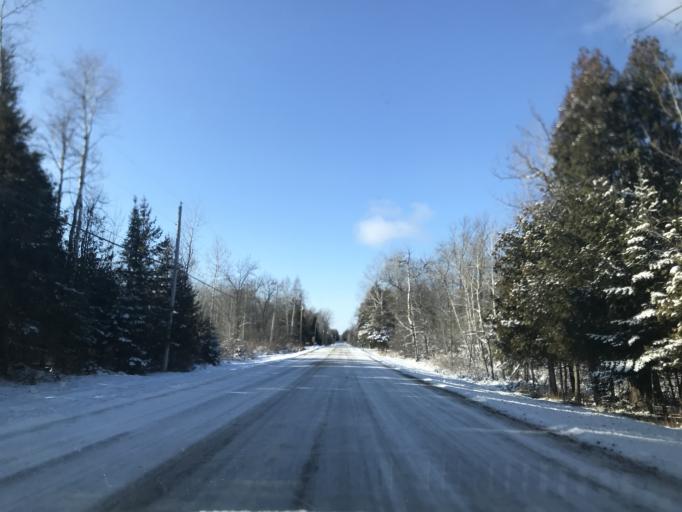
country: US
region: Wisconsin
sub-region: Door County
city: Sturgeon Bay
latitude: 44.8496
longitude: -87.4880
